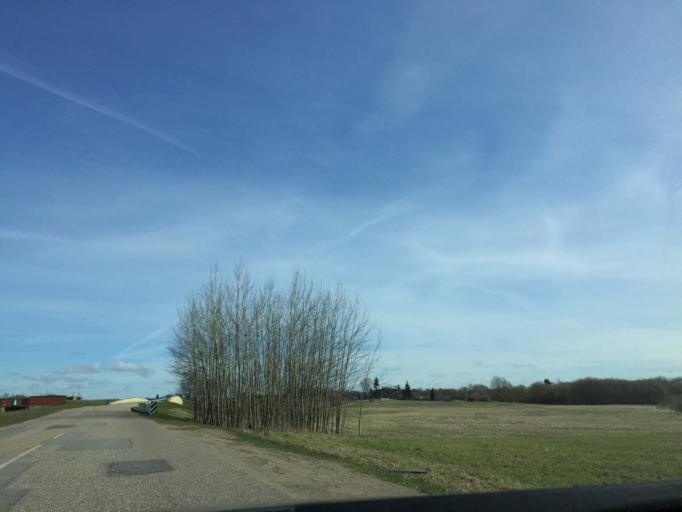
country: LT
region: Siauliu apskritis
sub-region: Siauliai
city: Siauliai
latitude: 56.0134
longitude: 23.4080
